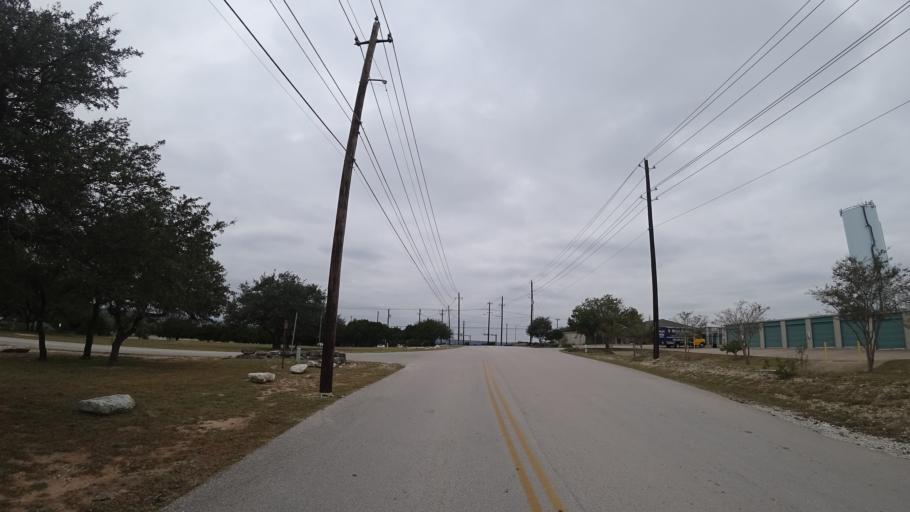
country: US
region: Texas
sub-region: Travis County
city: Lakeway
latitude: 30.3717
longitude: -97.9465
